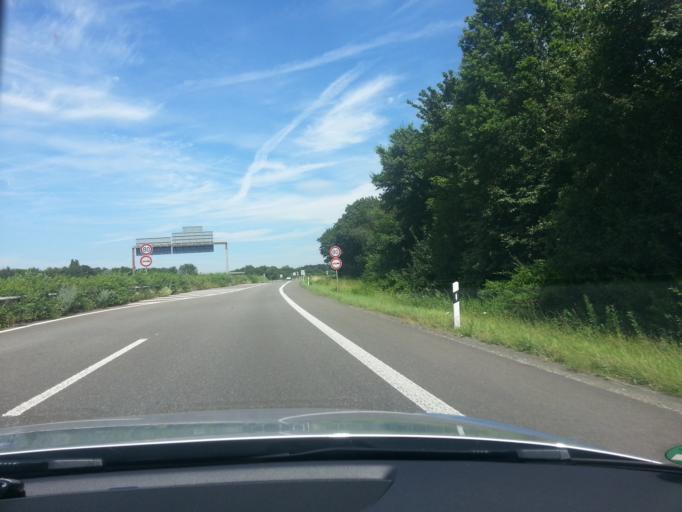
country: DE
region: Rheinland-Pfalz
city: Mutterstadt
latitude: 49.4593
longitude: 8.3609
